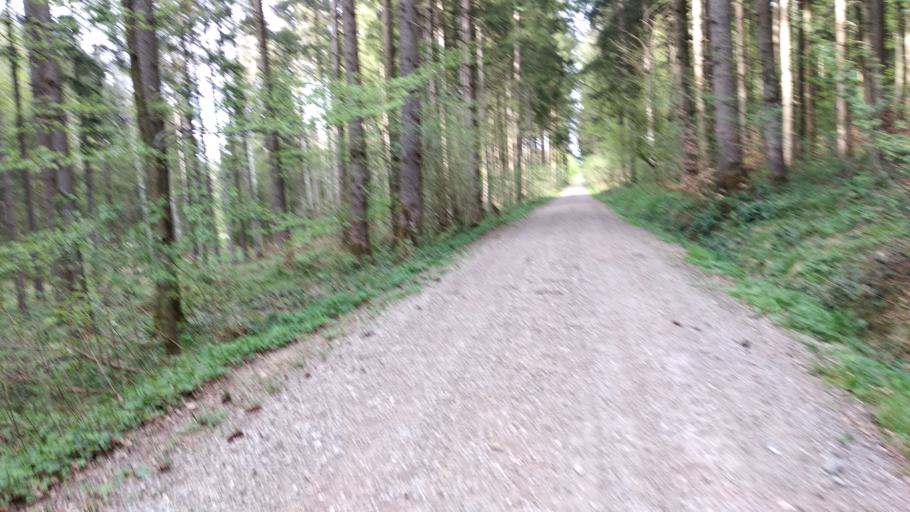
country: DE
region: Bavaria
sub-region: Swabia
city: Woringen
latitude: 47.9268
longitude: 10.1859
